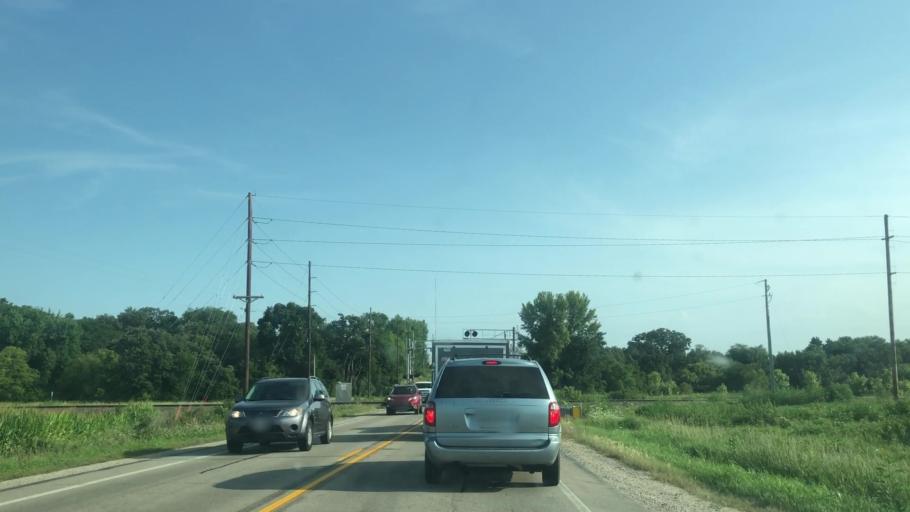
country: US
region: Iowa
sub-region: Marshall County
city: Marshalltown
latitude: 42.0303
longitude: -93.0001
